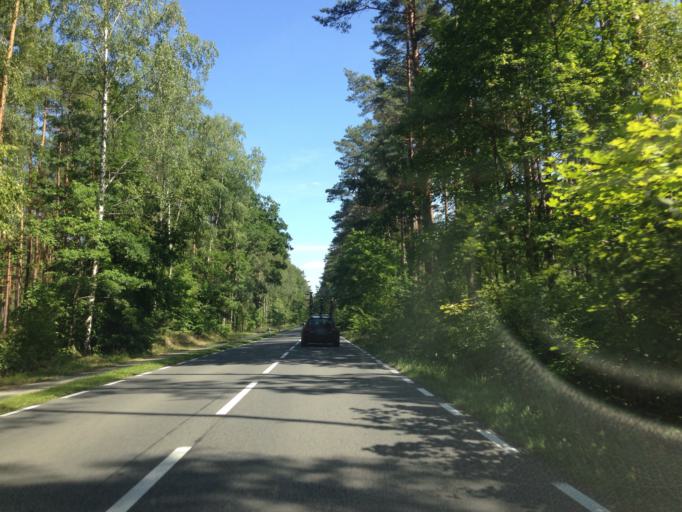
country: PL
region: Kujawsko-Pomorskie
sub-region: Powiat swiecki
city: Osie
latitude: 53.6077
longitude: 18.3124
